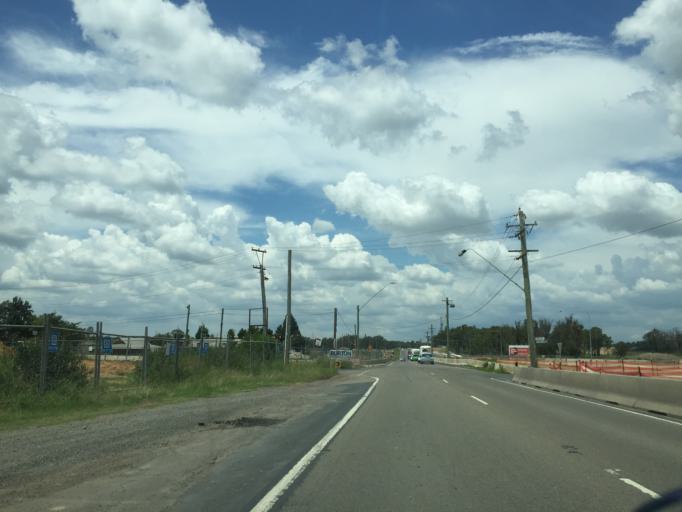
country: AU
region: New South Wales
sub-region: Blacktown
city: Hassall Grove
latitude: -33.7064
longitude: 150.8389
